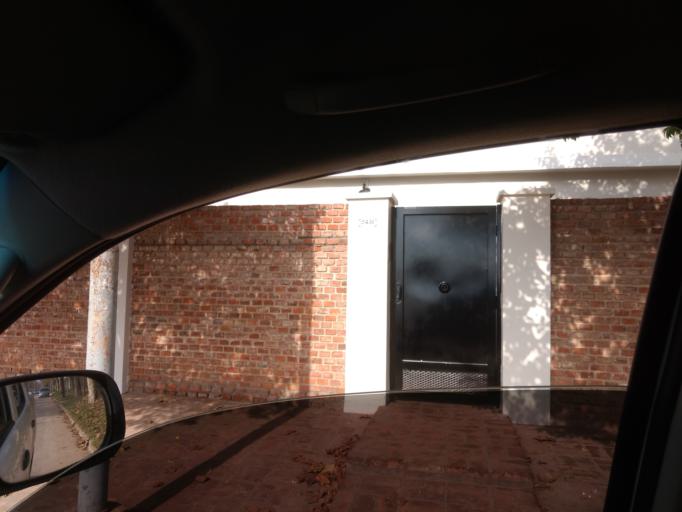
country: AR
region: Buenos Aires
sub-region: Partido de Lobos
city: Lobos
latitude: -35.1770
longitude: -59.0664
